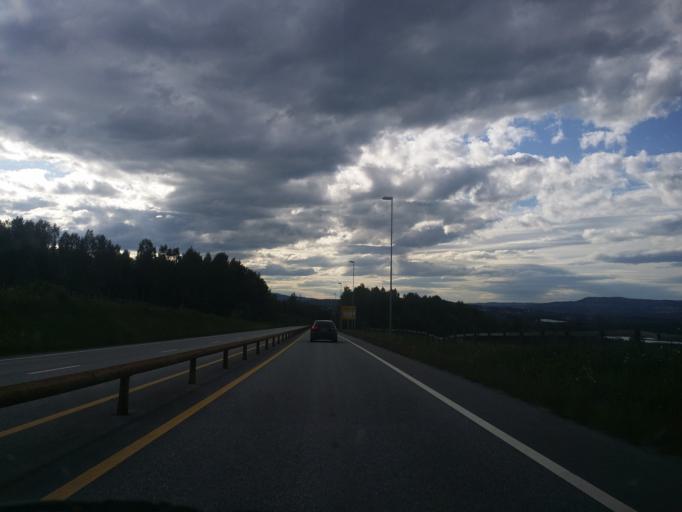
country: NO
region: Hedmark
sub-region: Hamar
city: Hamar
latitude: 60.7801
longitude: 11.1428
